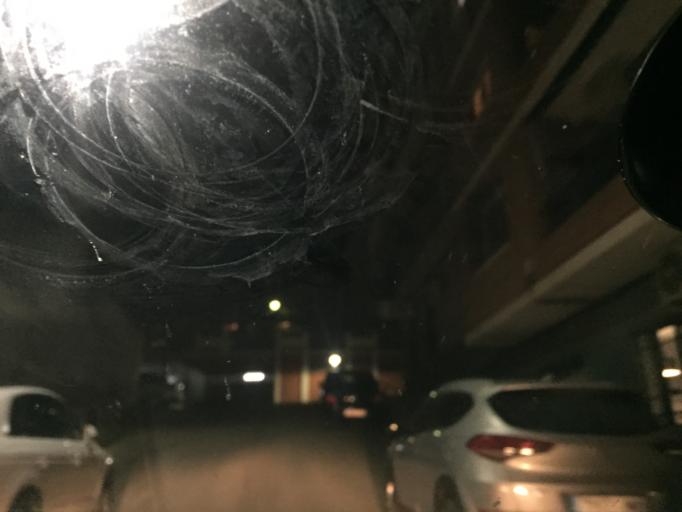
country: ES
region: Andalusia
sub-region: Provincia de Jaen
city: Jaen
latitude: 37.7772
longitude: -3.7975
